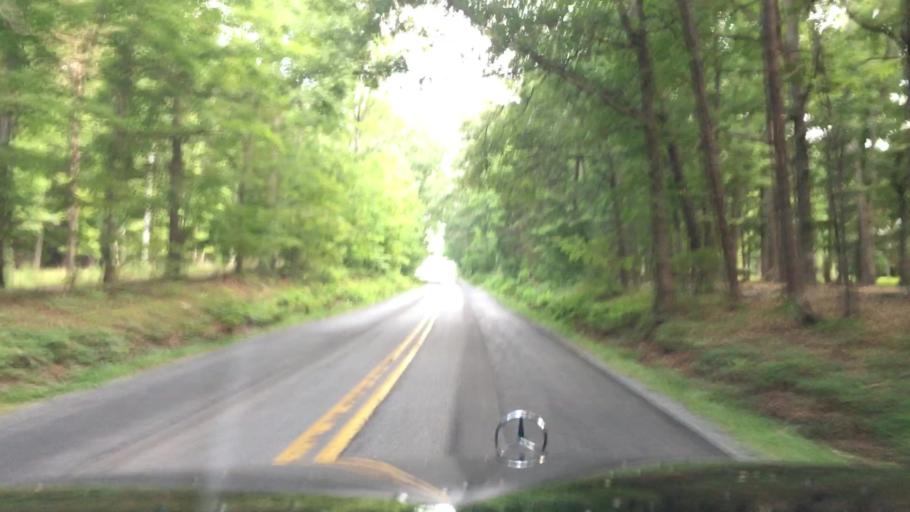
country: US
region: Virginia
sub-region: Campbell County
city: Timberlake
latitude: 37.2747
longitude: -79.3128
